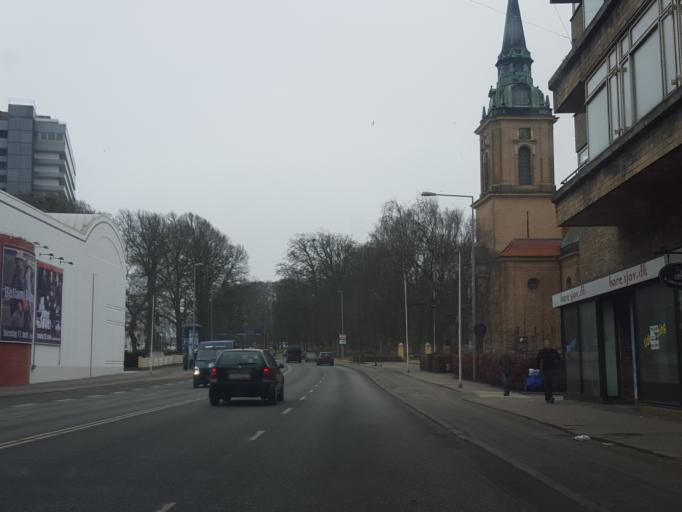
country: DK
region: North Denmark
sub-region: Alborg Kommune
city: Aalborg
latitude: 57.0440
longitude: 9.9116
